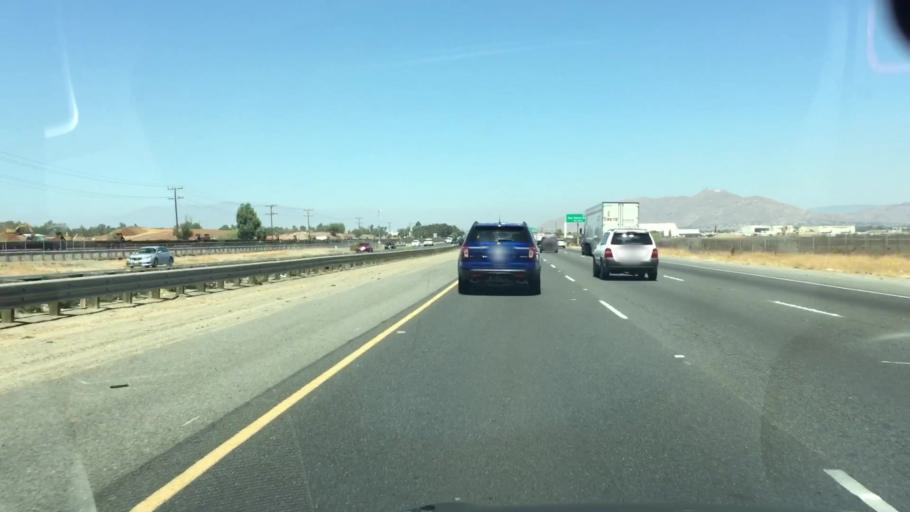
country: US
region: California
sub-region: Riverside County
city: March Air Force Base
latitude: 33.8735
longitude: -117.2643
